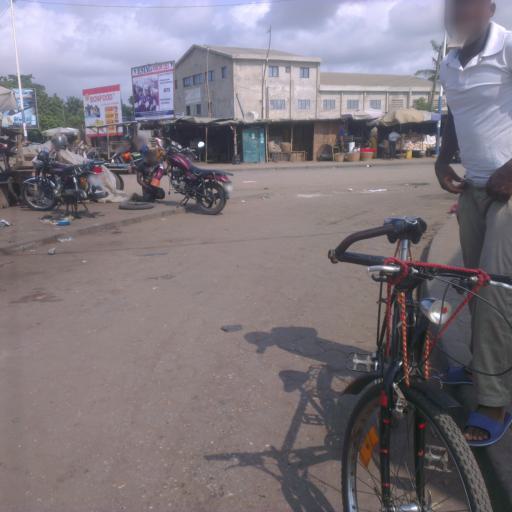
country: TG
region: Maritime
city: Lome
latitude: 6.1538
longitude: 1.2675
